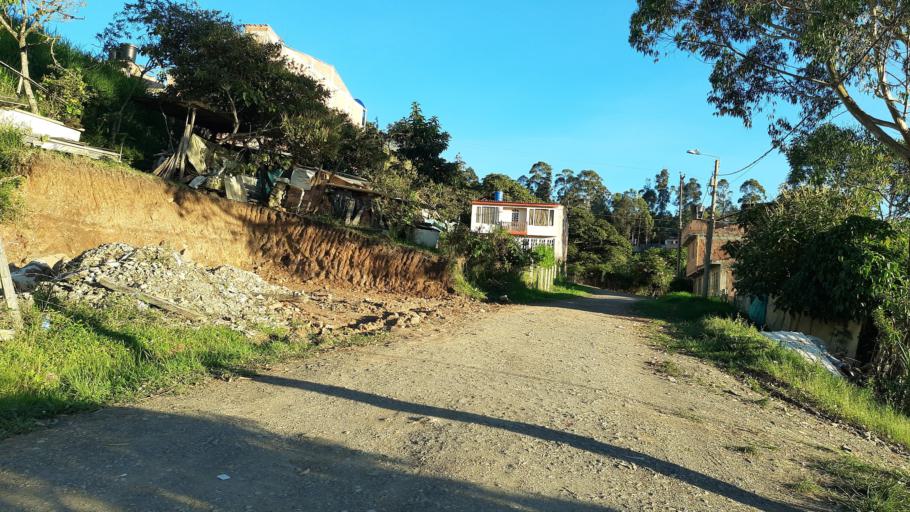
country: CO
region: Boyaca
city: Garagoa
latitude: 5.0813
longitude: -73.3685
